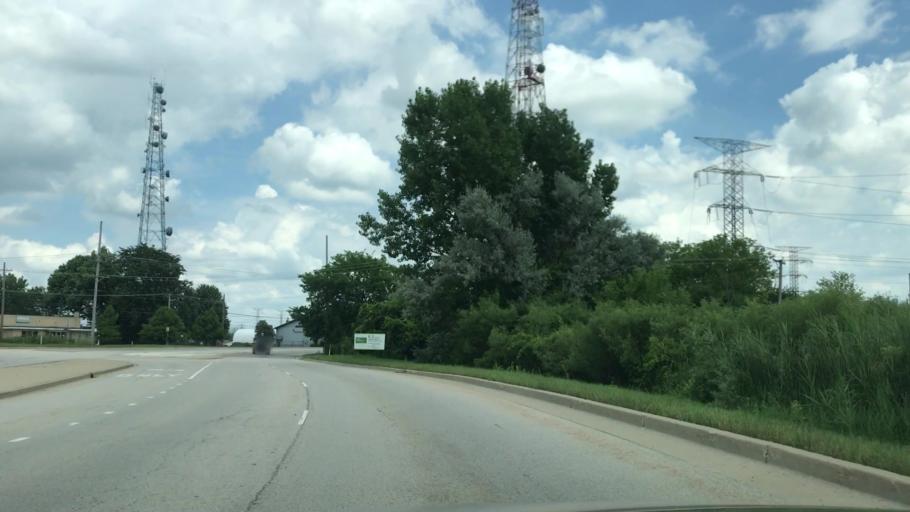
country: US
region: Illinois
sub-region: DuPage County
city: Warrenville
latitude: 41.7983
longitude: -88.2385
